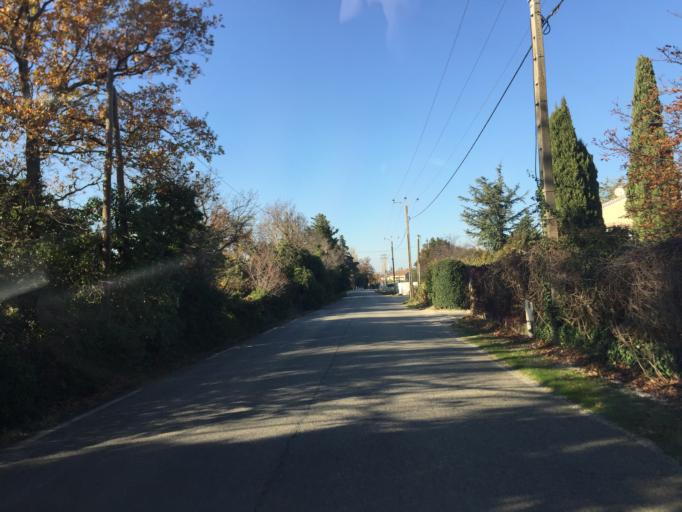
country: FR
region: Provence-Alpes-Cote d'Azur
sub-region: Departement du Vaucluse
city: Camaret-sur-Aigues
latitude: 44.1571
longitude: 4.8780
